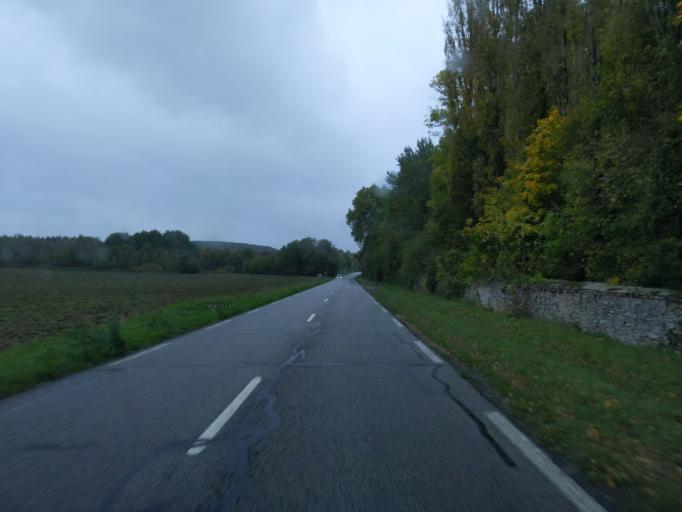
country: FR
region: Ile-de-France
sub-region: Departement des Yvelines
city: Dampierre-en-Yvelines
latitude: 48.6925
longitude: 1.9754
